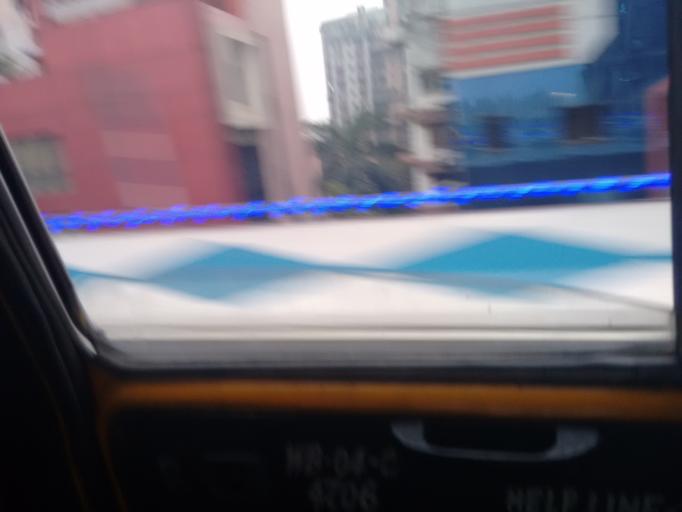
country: IN
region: West Bengal
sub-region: Kolkata
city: Kolkata
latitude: 22.5418
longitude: 88.3856
